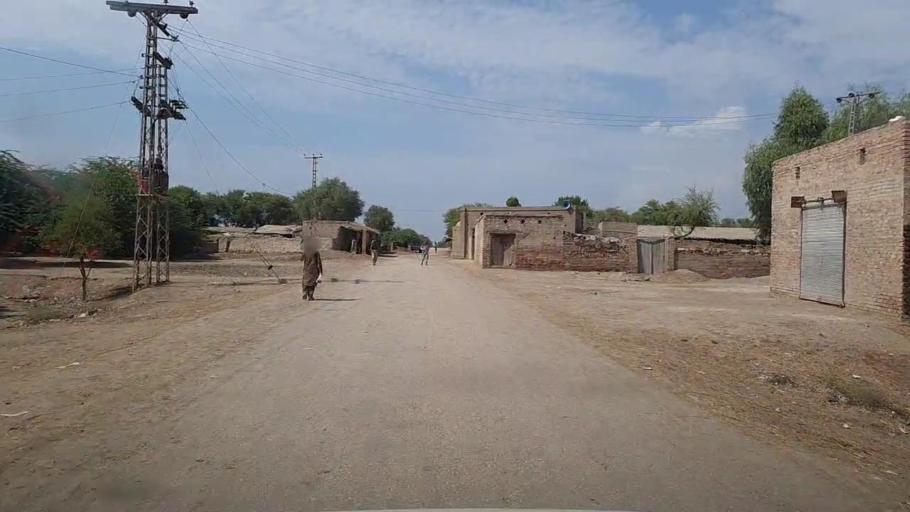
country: PK
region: Sindh
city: Thul
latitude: 28.2466
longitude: 68.8093
